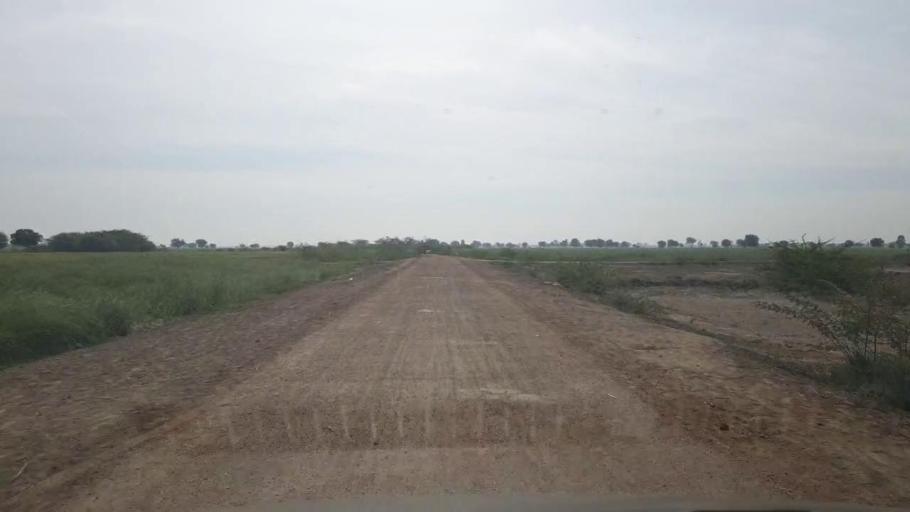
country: PK
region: Sindh
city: Umarkot
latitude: 25.3607
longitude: 69.6342
